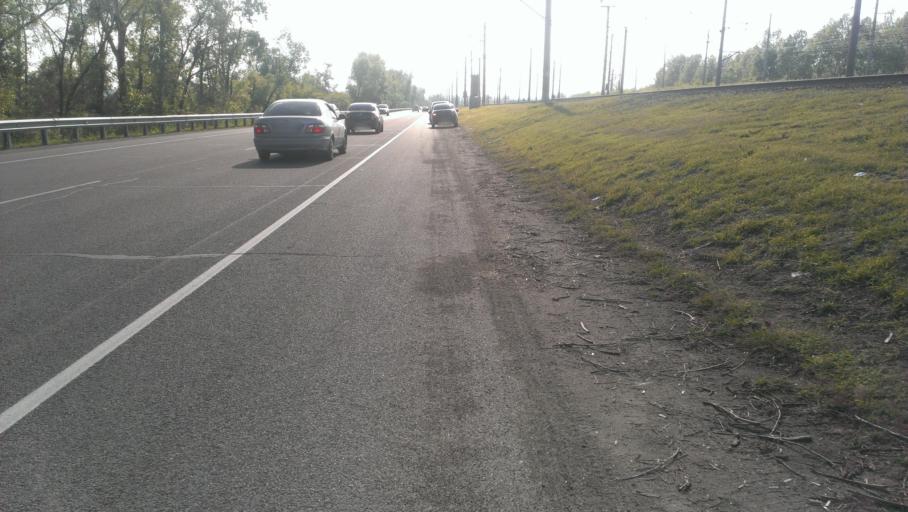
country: RU
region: Altai Krai
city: Novoaltaysk
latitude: 53.3691
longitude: 83.8603
